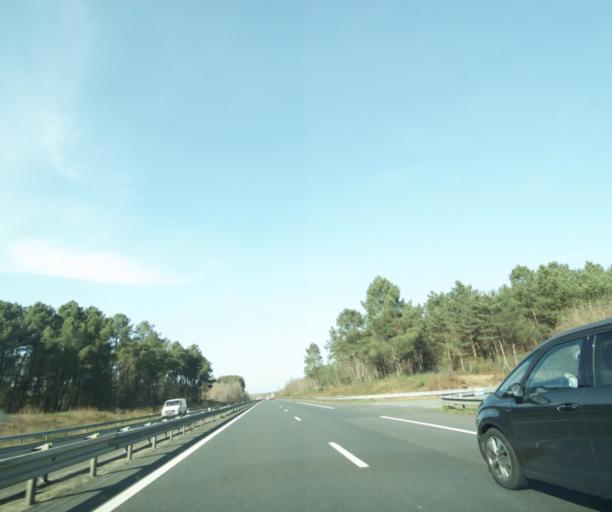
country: FR
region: Centre
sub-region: Departement du Loir-et-Cher
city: Nouan-le-Fuzelier
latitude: 47.5353
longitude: 2.0051
